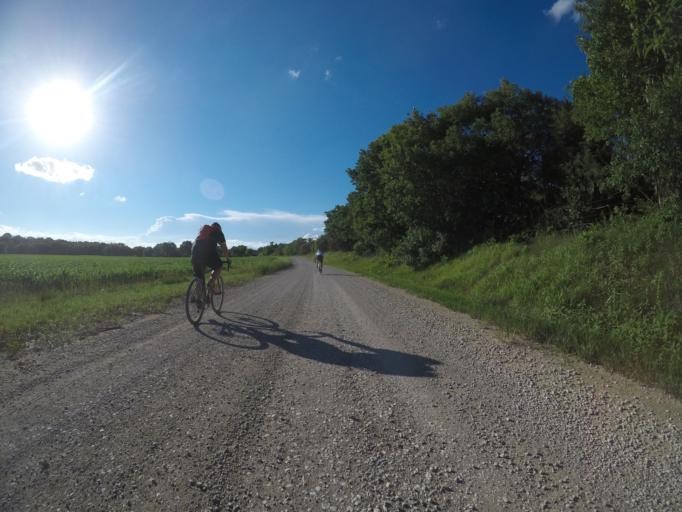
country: US
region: Kansas
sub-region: Riley County
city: Ogden
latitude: 39.2424
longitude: -96.7317
